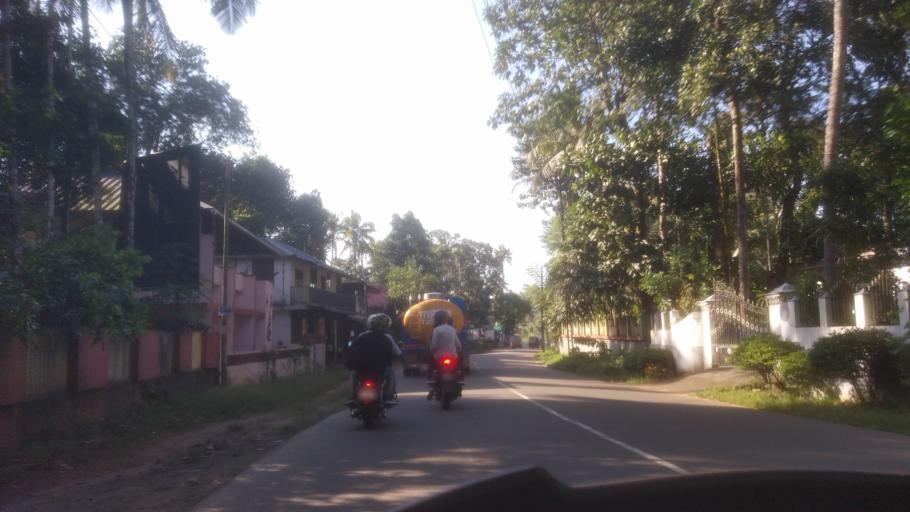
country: IN
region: Kerala
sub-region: Ernakulam
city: Ramamangalam
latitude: 9.9748
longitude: 76.4995
